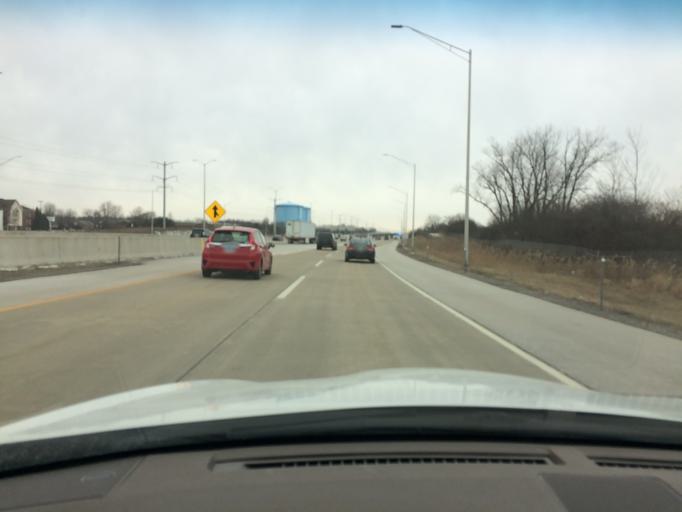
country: US
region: Illinois
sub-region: Cook County
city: South Barrington
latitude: 42.0671
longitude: -88.1478
